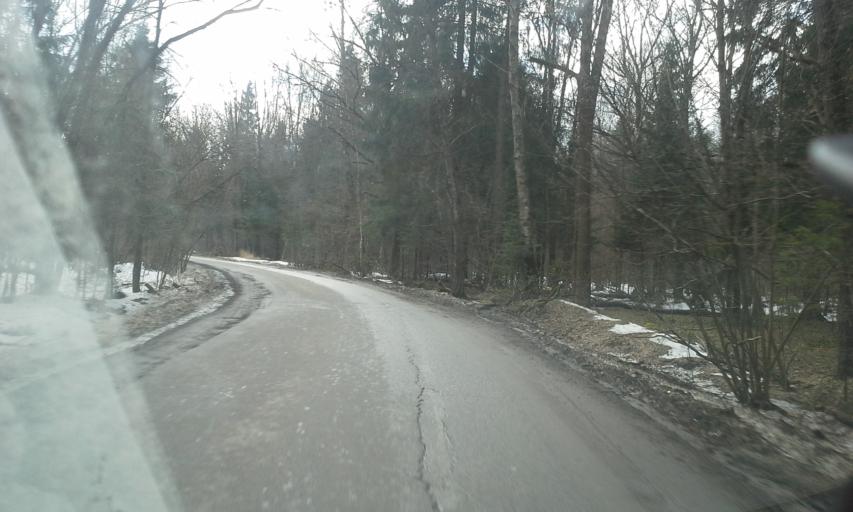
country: RU
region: Moscow
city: Tolstopal'tsevo
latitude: 55.6116
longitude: 37.2449
